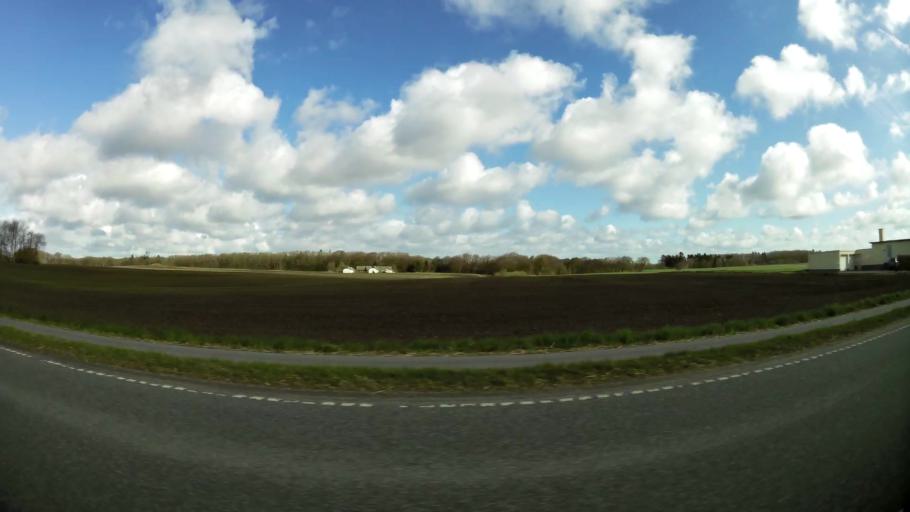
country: DK
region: North Denmark
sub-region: Mariagerfjord Kommune
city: Hobro
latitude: 56.6256
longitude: 9.8500
